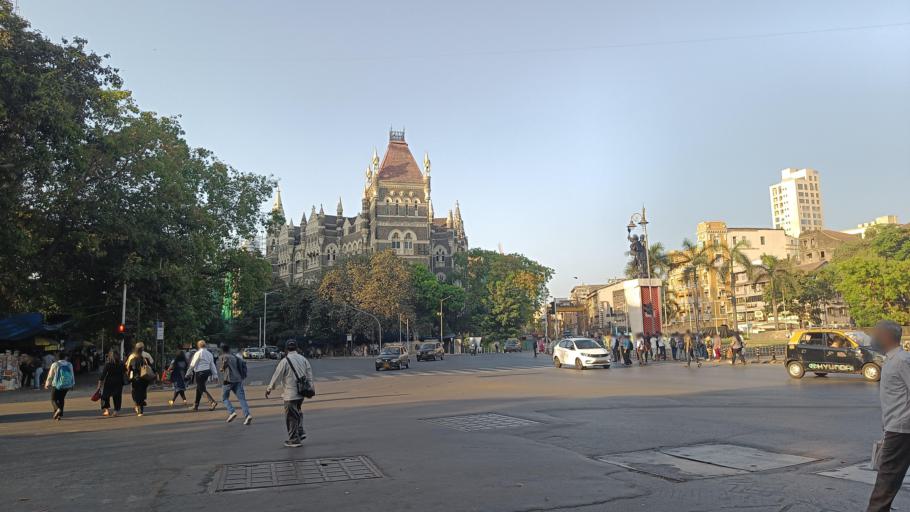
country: IN
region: Maharashtra
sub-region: Raigarh
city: Uran
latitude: 18.9323
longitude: 72.8312
